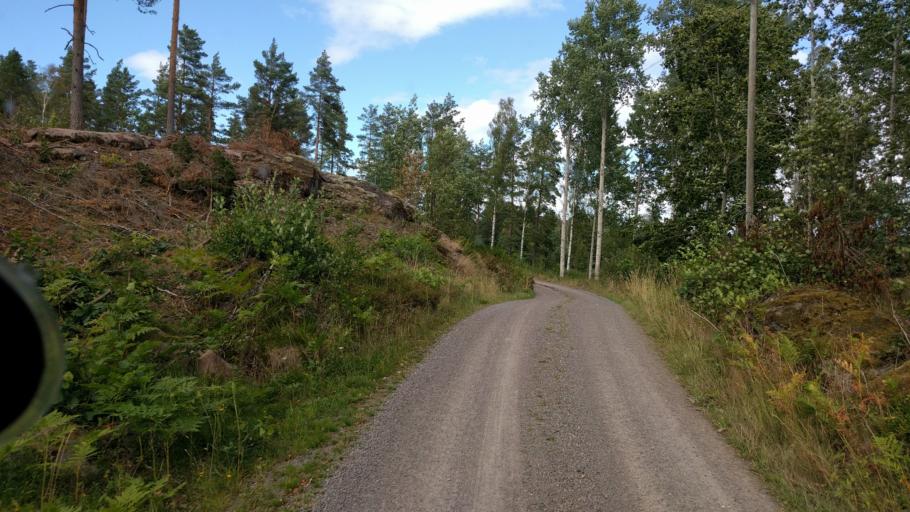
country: SE
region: Kalmar
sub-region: Vasterviks Kommun
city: Ankarsrum
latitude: 57.7277
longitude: 16.0946
